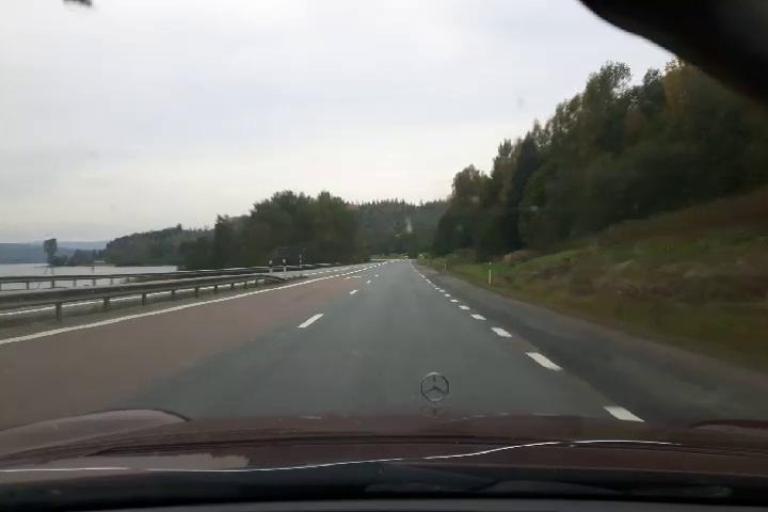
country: SE
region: Vaesternorrland
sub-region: Kramfors Kommun
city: Nordingra
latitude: 63.0078
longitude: 18.2710
